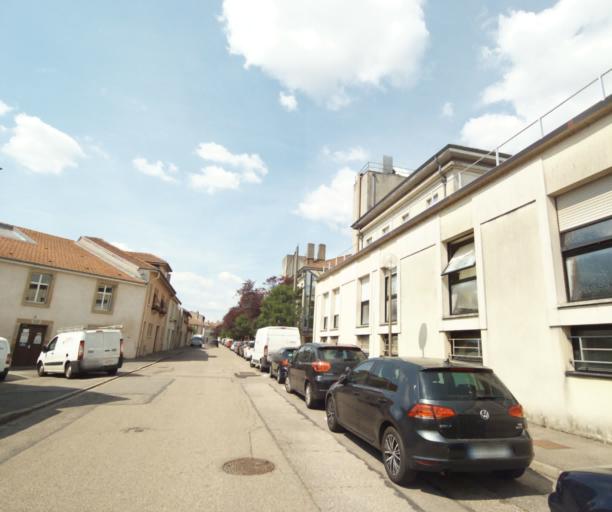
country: FR
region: Lorraine
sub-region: Departement de Meurthe-et-Moselle
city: Luneville
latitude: 48.5879
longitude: 6.4909
